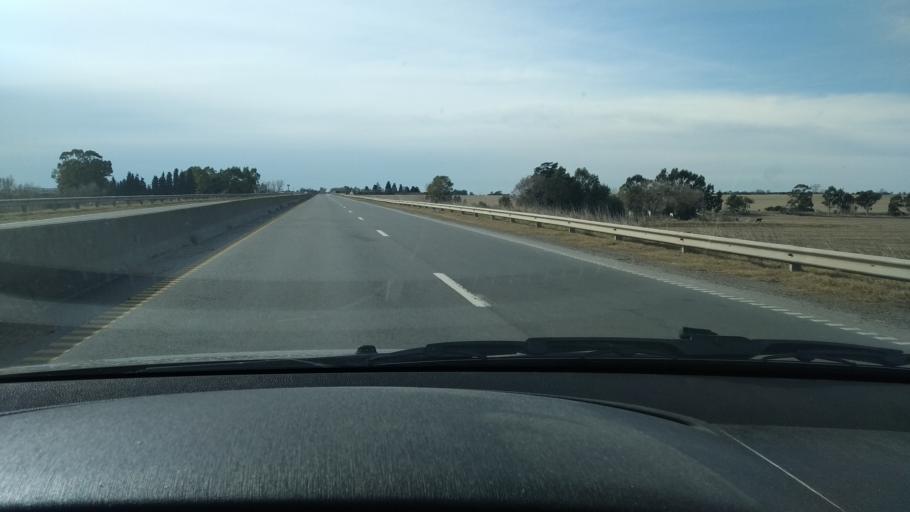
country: AR
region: Buenos Aires
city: Olavarria
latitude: -36.8839
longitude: -60.1510
